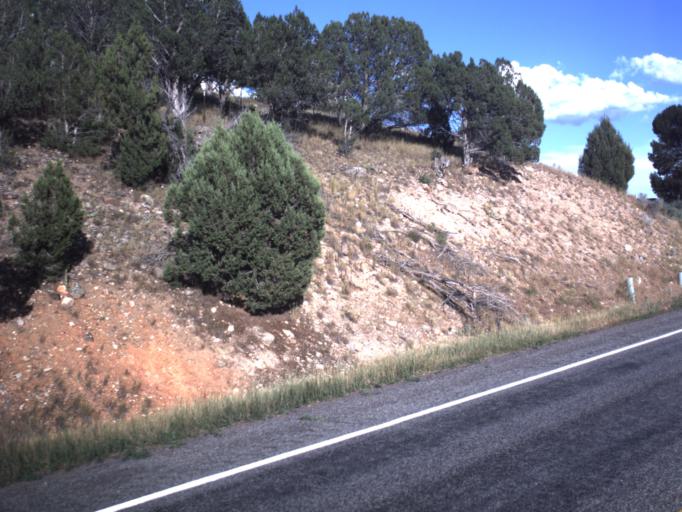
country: US
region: Utah
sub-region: Utah County
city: Woodland Hills
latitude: 39.8770
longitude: -111.5408
